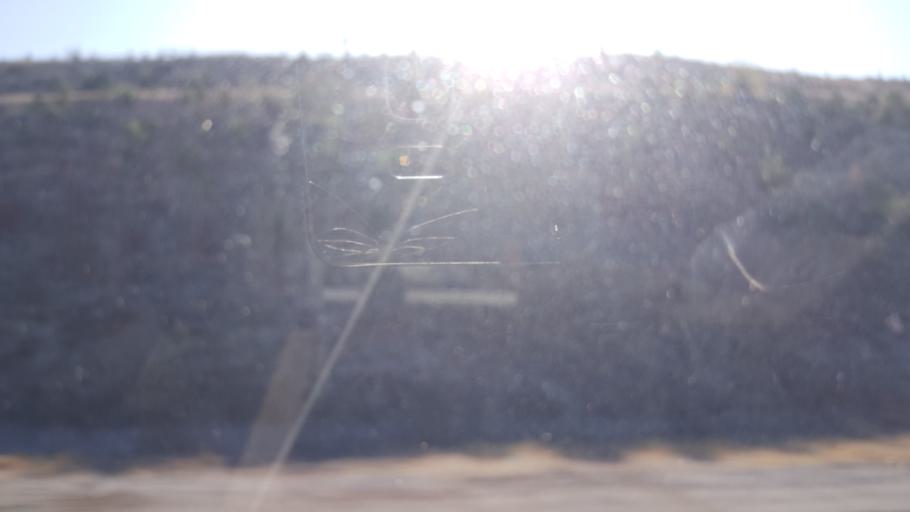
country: TR
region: Ankara
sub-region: Goelbasi
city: Golbasi
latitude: 39.8287
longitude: 32.8832
